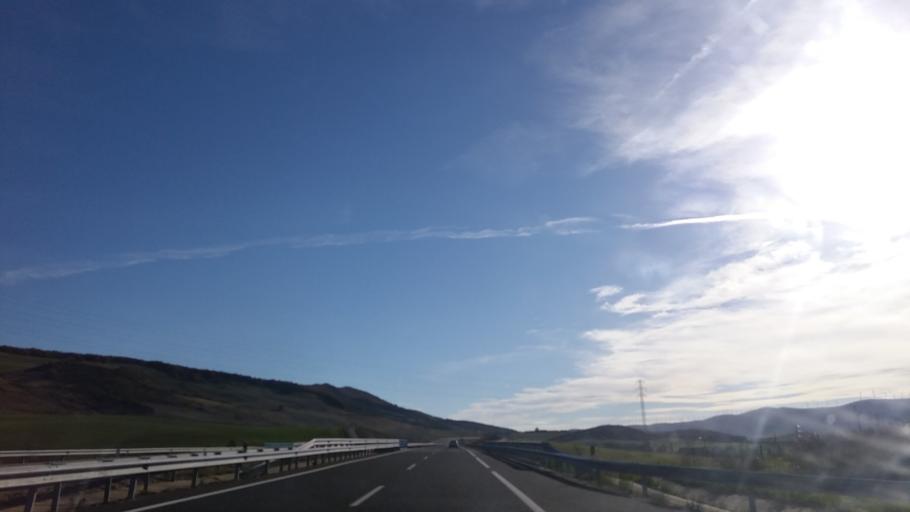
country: ES
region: Navarre
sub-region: Provincia de Navarra
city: Monreal
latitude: 42.7110
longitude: -1.5068
